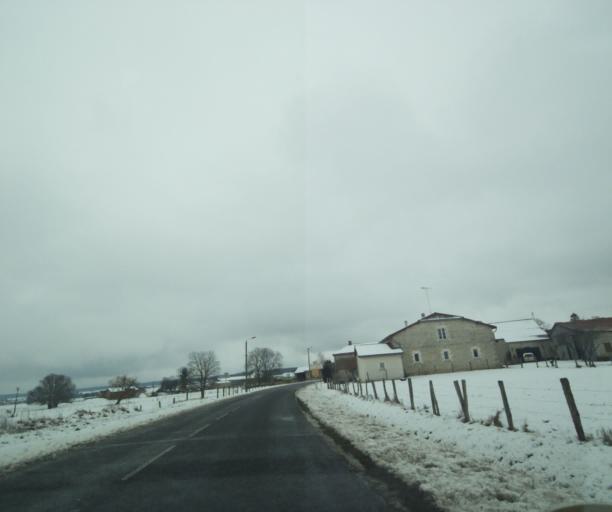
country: FR
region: Champagne-Ardenne
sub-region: Departement de la Haute-Marne
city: Montier-en-Der
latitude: 48.4232
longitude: 4.8185
